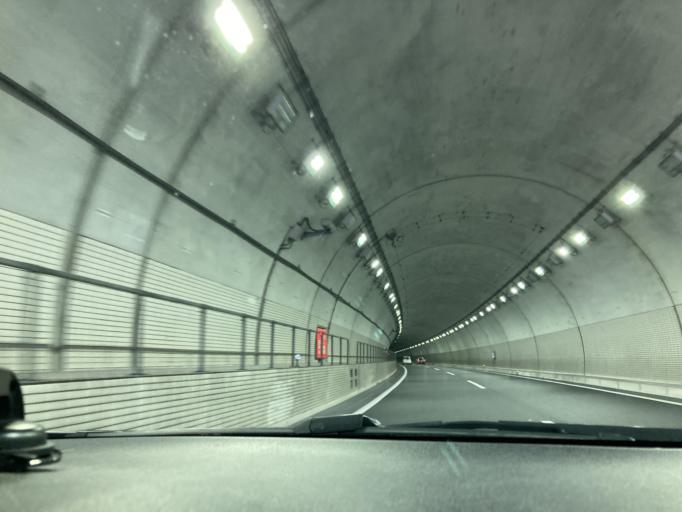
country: JP
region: Okinawa
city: Tomigusuku
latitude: 26.1713
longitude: 127.6810
